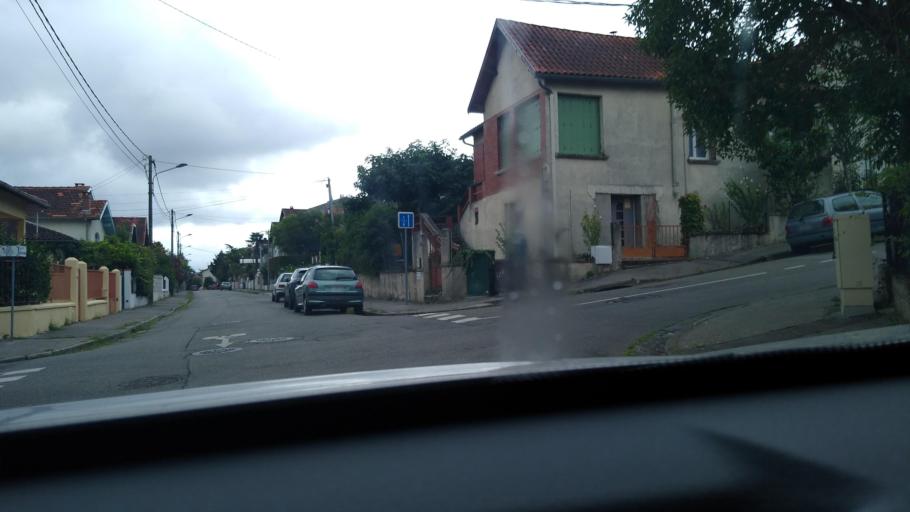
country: FR
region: Midi-Pyrenees
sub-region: Departement de la Haute-Garonne
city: Toulouse
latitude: 43.6260
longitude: 1.4621
